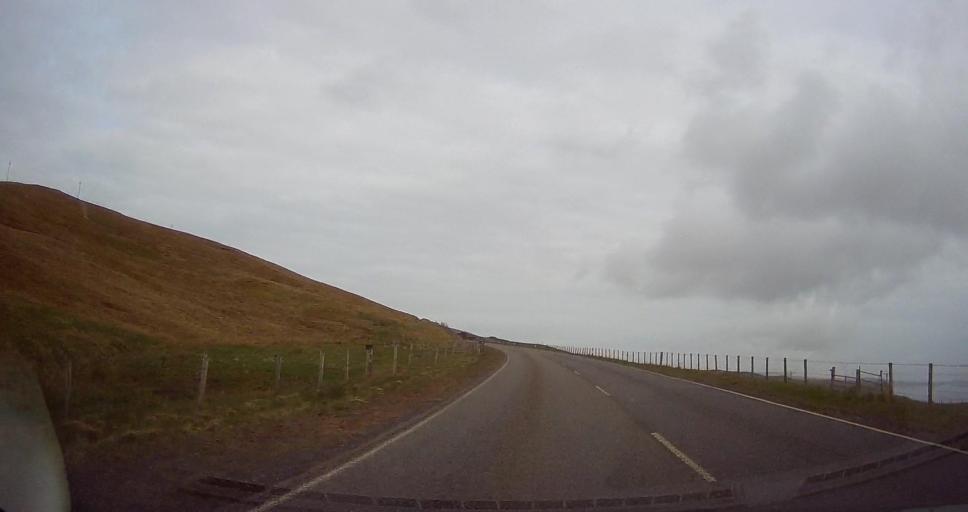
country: GB
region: Scotland
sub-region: Shetland Islands
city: Sandwick
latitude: 60.0632
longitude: -1.2215
